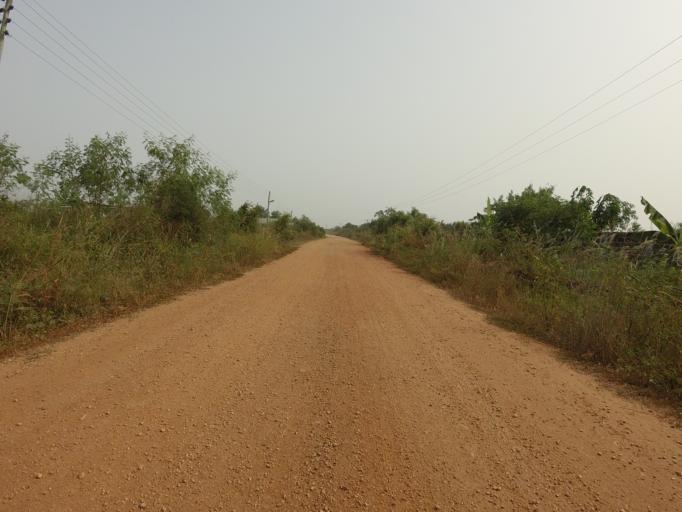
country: GH
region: Volta
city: Anloga
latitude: 5.9830
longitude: 0.6020
